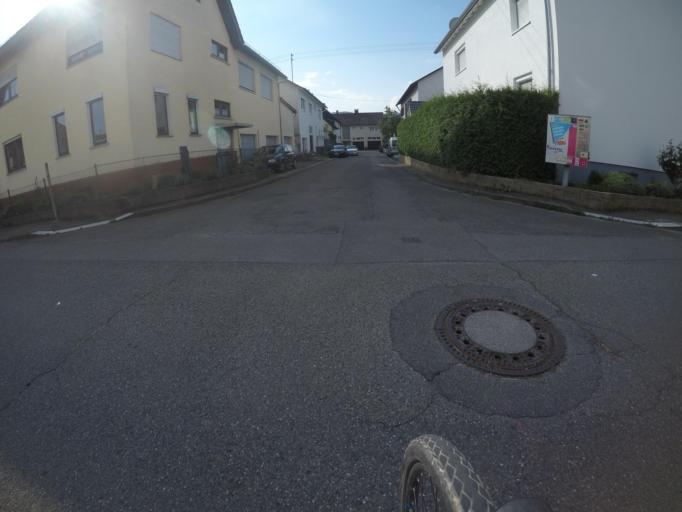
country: DE
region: Baden-Wuerttemberg
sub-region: Tuebingen Region
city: Metzingen
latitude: 48.5314
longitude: 9.3078
